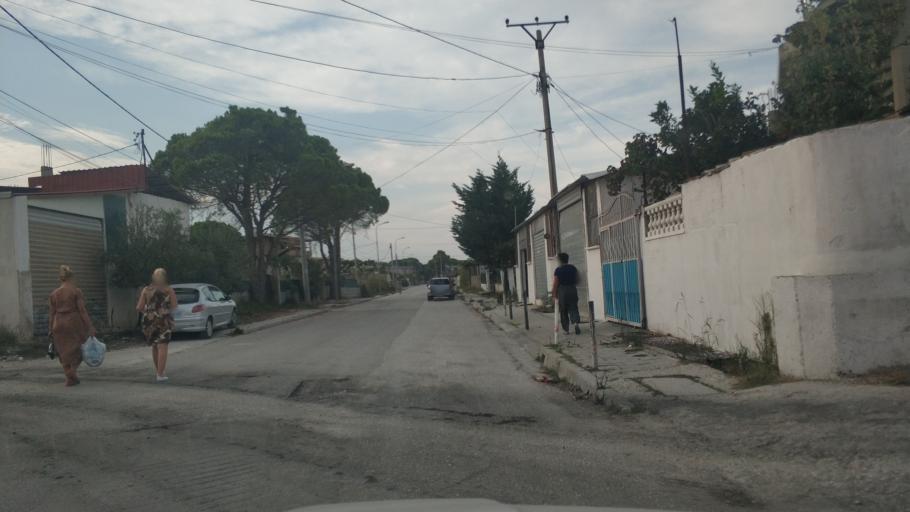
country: AL
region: Vlore
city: Vlore
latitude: 40.4641
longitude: 19.4666
